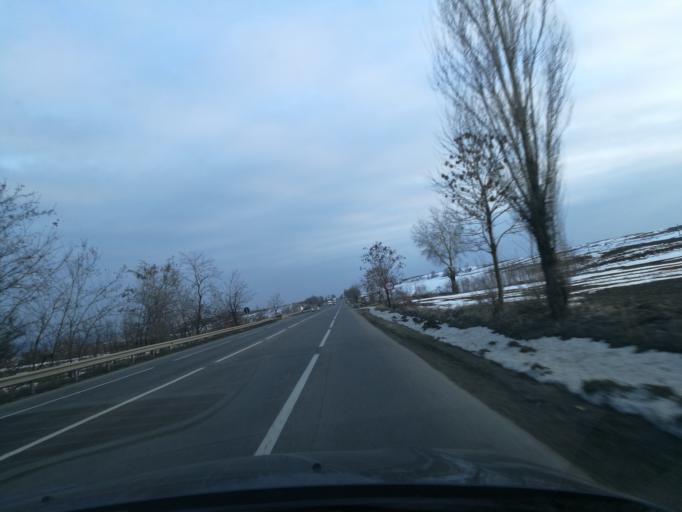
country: RO
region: Bacau
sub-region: Comuna Valea Seaca
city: Valea Seaca
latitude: 46.2673
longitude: 27.0663
